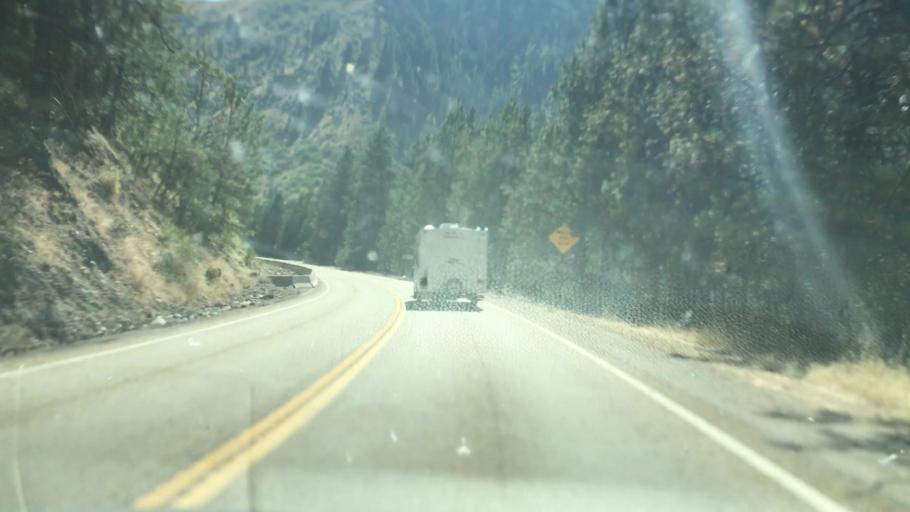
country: US
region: Idaho
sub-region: Boise County
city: Idaho City
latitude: 44.0831
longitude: -116.1187
